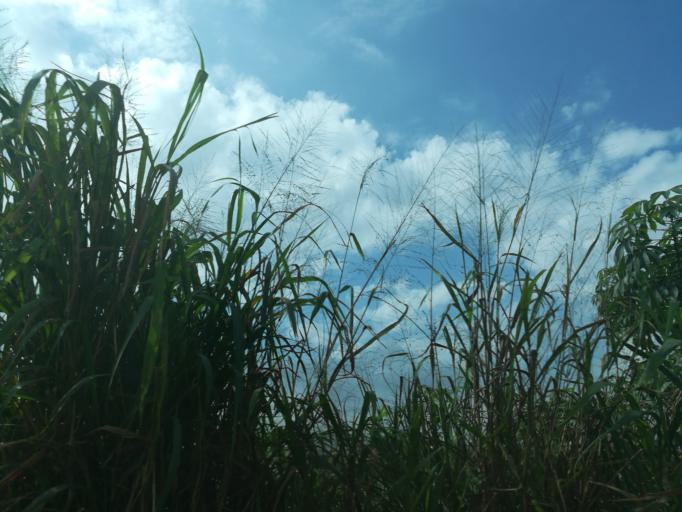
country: NG
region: Lagos
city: Ikorodu
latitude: 6.6318
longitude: 3.5313
